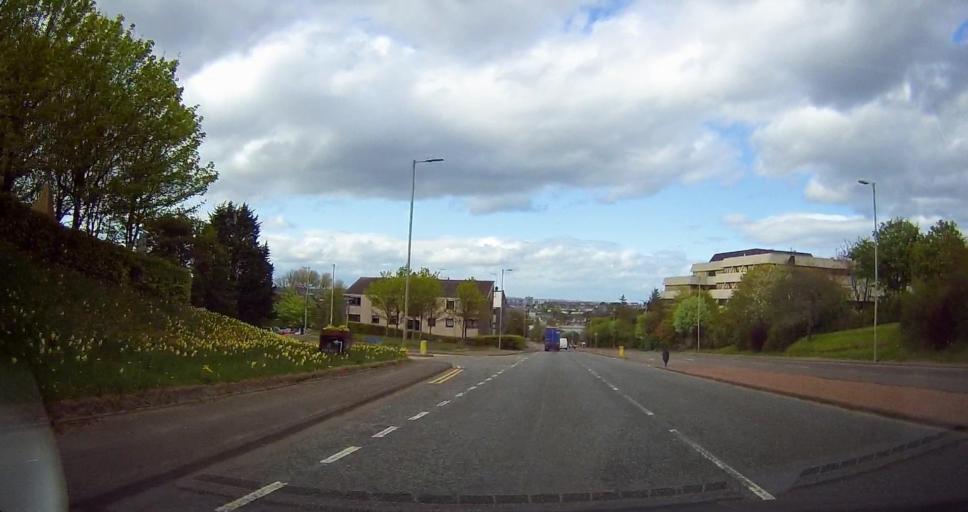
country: GB
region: Scotland
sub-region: Aberdeen City
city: Aberdeen
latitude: 57.1194
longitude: -2.0888
